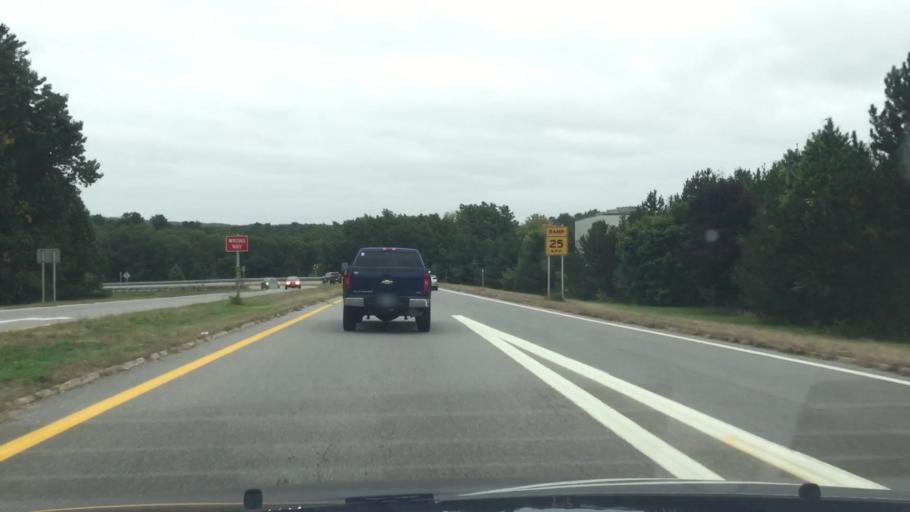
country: US
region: New Hampshire
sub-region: Hillsborough County
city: Hudson
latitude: 42.7207
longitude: -71.4419
